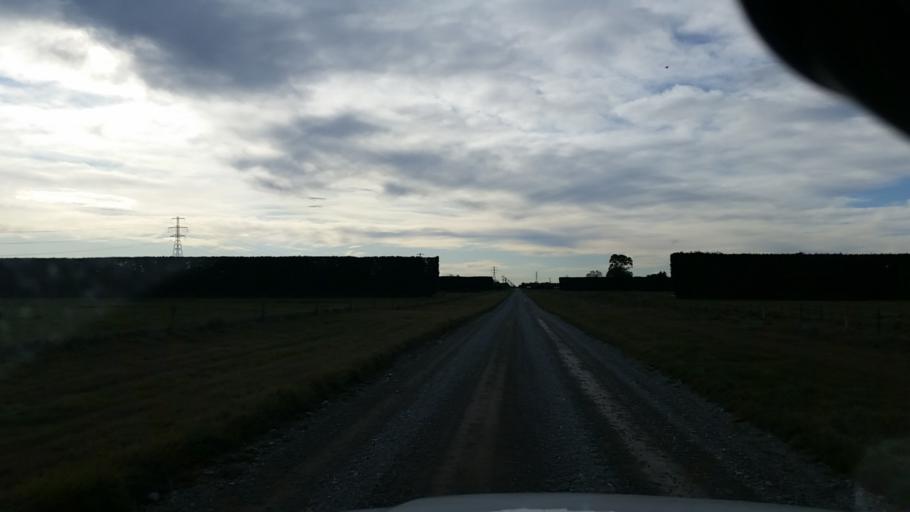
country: NZ
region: Canterbury
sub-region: Ashburton District
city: Tinwald
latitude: -44.0405
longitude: 171.4872
